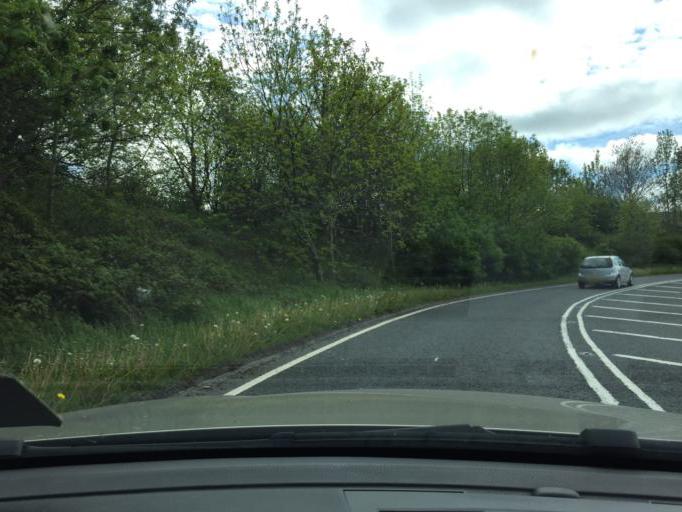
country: GB
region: Northern Ireland
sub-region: Craigavon District
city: Craigavon
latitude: 54.4426
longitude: -6.4153
